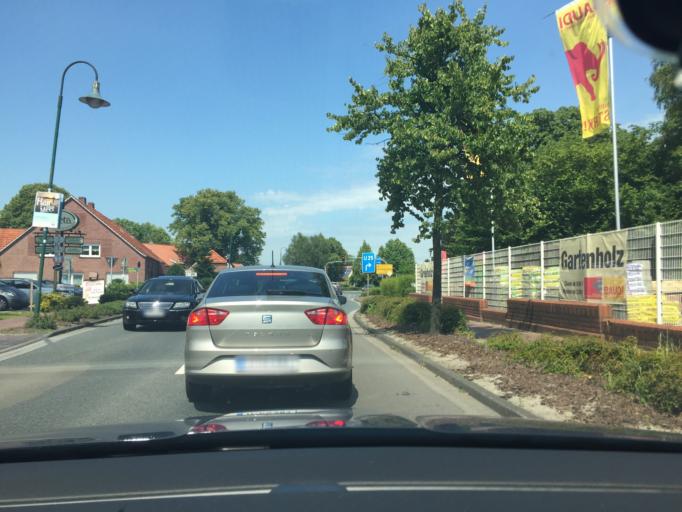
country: DE
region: Lower Saxony
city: Hesel
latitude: 53.3045
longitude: 7.5938
